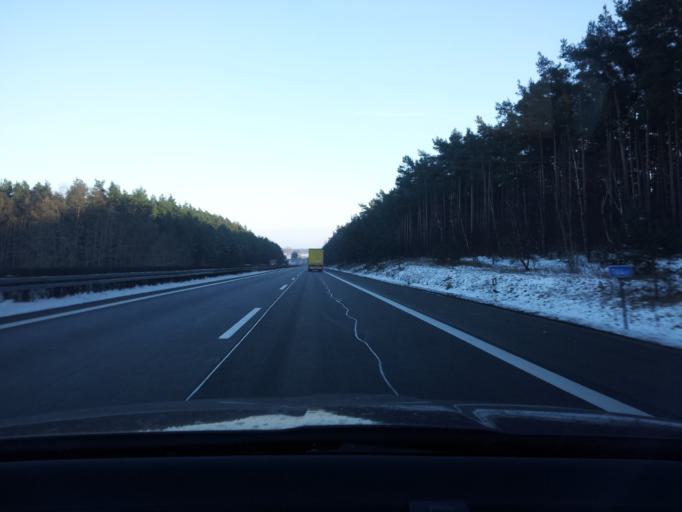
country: DE
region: Brandenburg
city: Heiligengrabe
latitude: 53.1713
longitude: 12.3392
